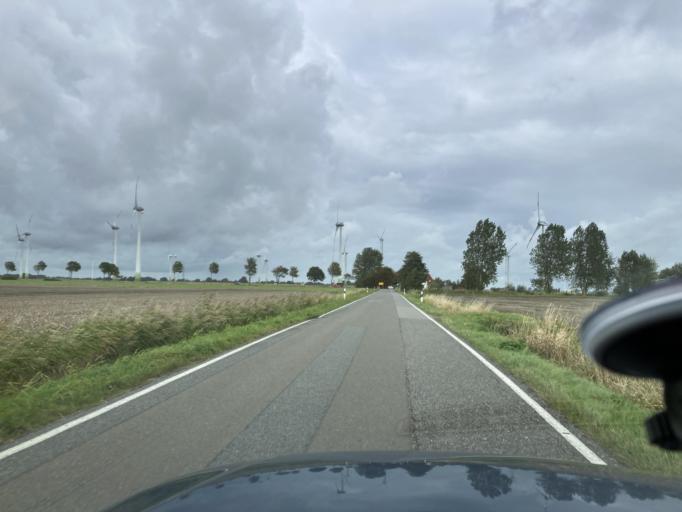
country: DE
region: Schleswig-Holstein
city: Wesselburener Deichhausen
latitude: 54.1831
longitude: 8.9496
